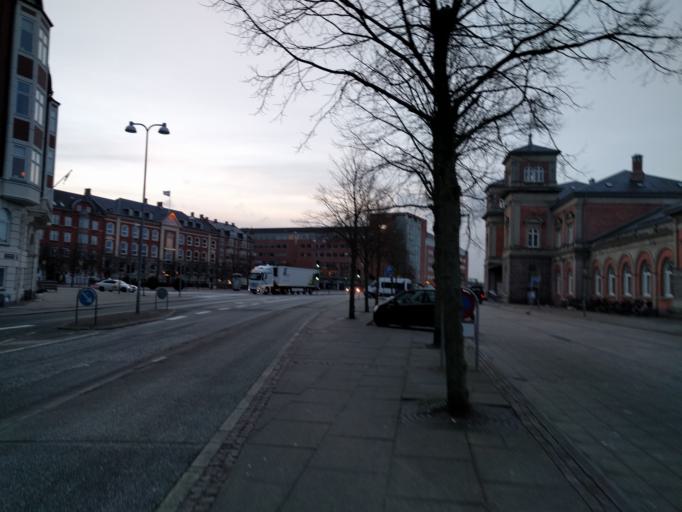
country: DK
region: North Denmark
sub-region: Alborg Kommune
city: Aalborg
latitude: 57.0440
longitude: 9.9169
